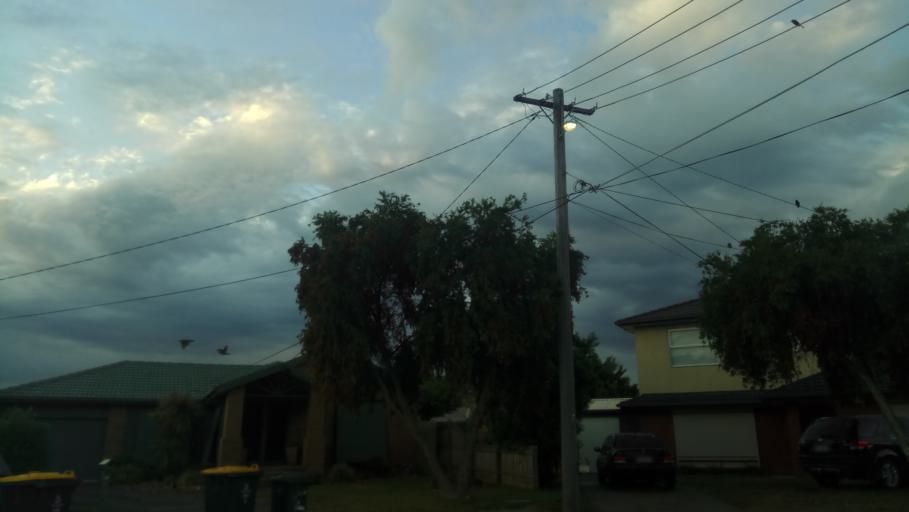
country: AU
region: Victoria
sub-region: Hobsons Bay
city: Altona Meadows
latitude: -37.8833
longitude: 144.7750
